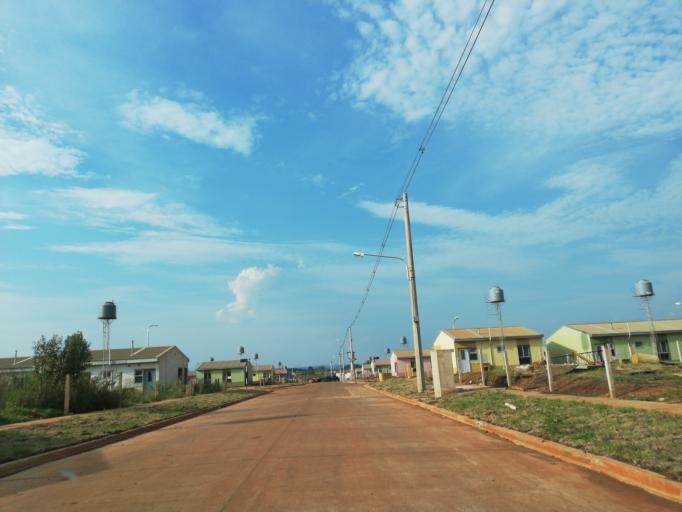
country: AR
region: Misiones
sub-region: Departamento de Capital
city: Posadas
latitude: -27.4003
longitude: -55.9907
